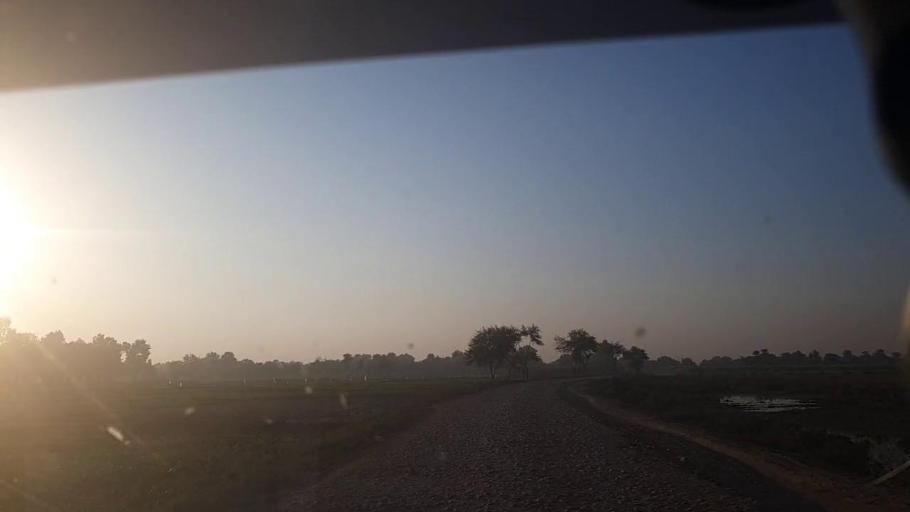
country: PK
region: Sindh
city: Sobhadero
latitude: 27.3614
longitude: 68.4167
